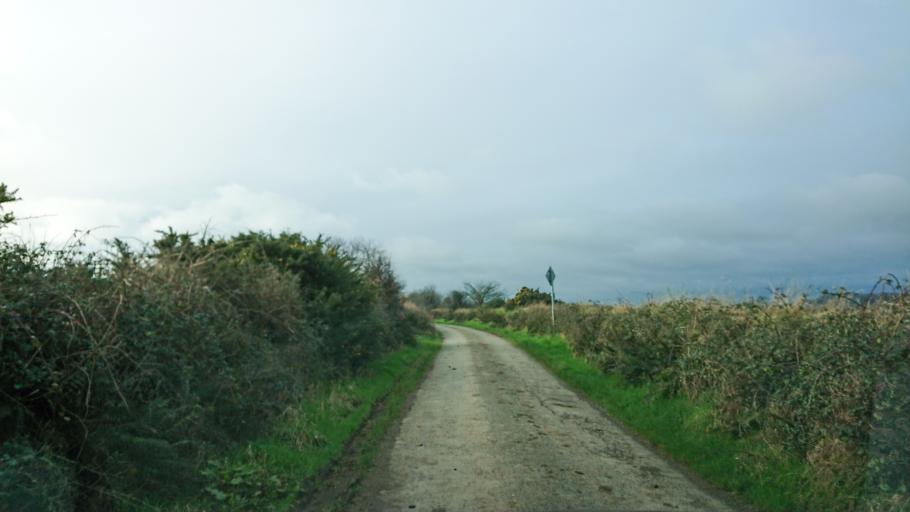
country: IE
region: Munster
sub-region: Waterford
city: Tra Mhor
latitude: 52.1996
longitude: -7.1656
